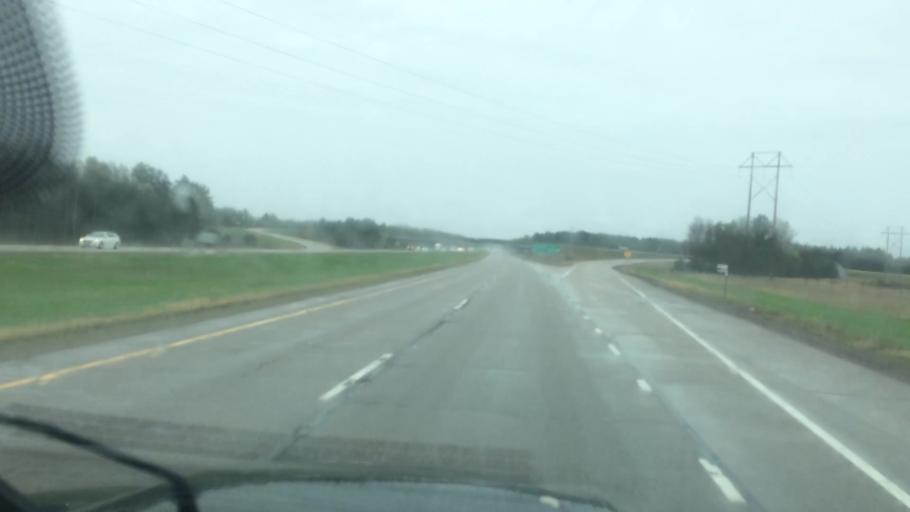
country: US
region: Wisconsin
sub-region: Portage County
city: Stevens Point
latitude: 44.5735
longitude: -89.6013
